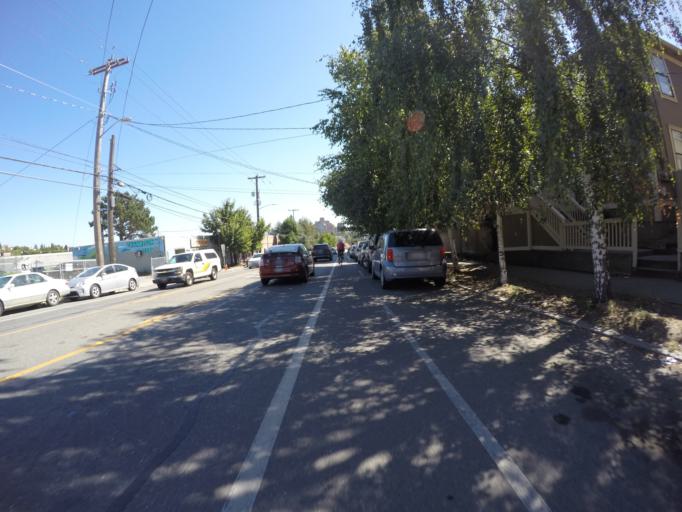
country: US
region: Washington
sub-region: King County
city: Seattle
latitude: 47.6025
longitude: -122.3169
